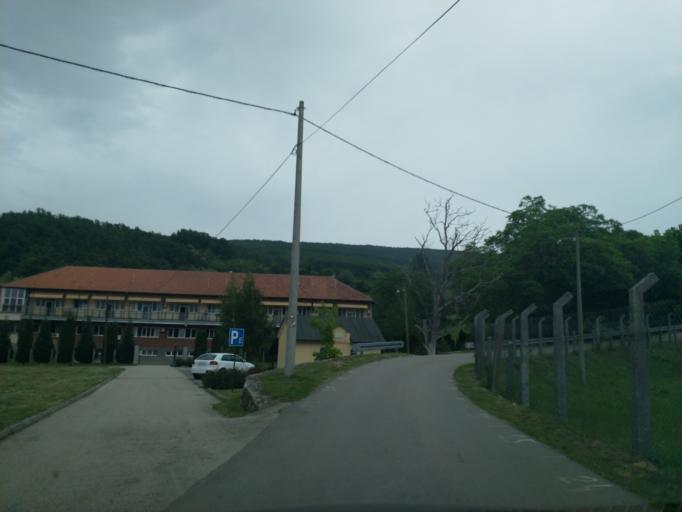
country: RS
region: Central Serbia
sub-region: Pomoravski Okrug
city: Paracin
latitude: 43.8568
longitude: 21.5980
